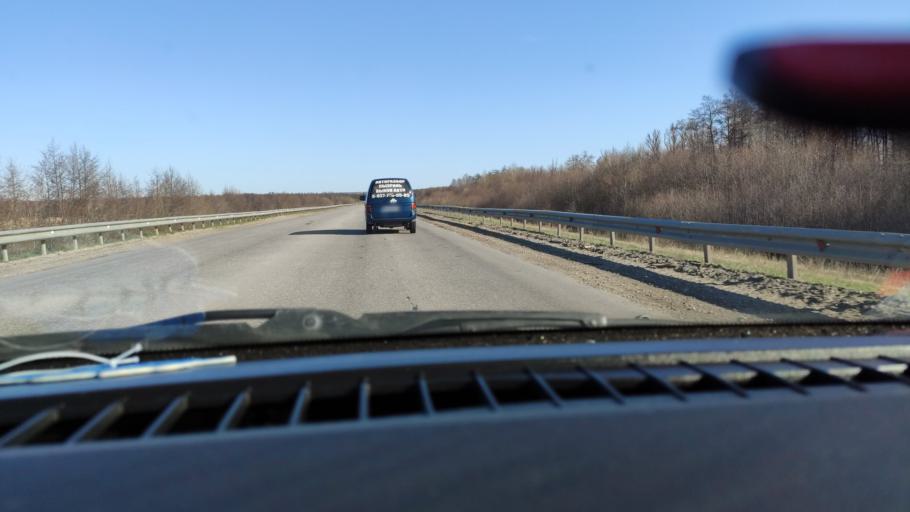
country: RU
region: Samara
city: Varlamovo
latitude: 53.1362
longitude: 48.2865
